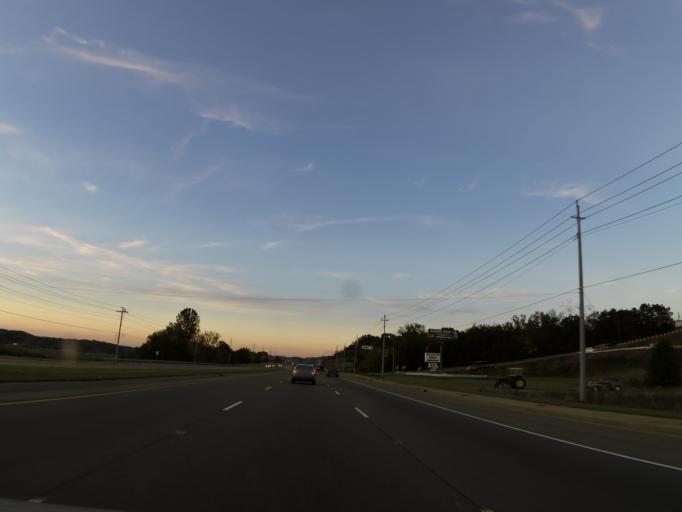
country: US
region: Tennessee
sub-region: Sevier County
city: Sevierville
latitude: 35.8941
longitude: -83.5808
